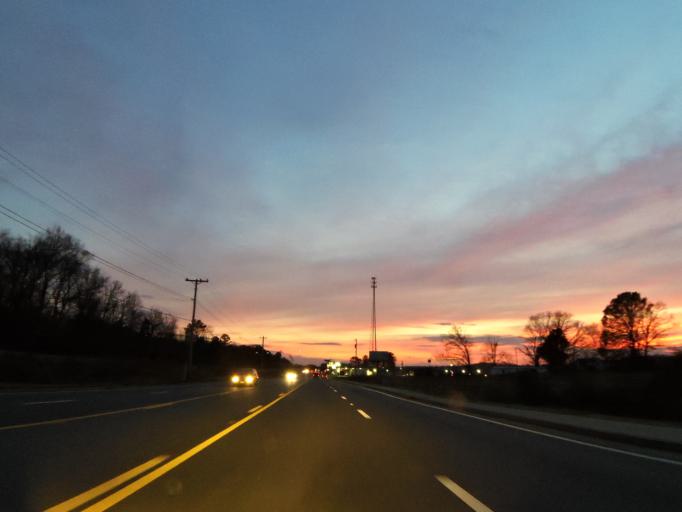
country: US
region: Tennessee
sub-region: Polk County
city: Benton
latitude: 35.1334
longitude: -84.7139
